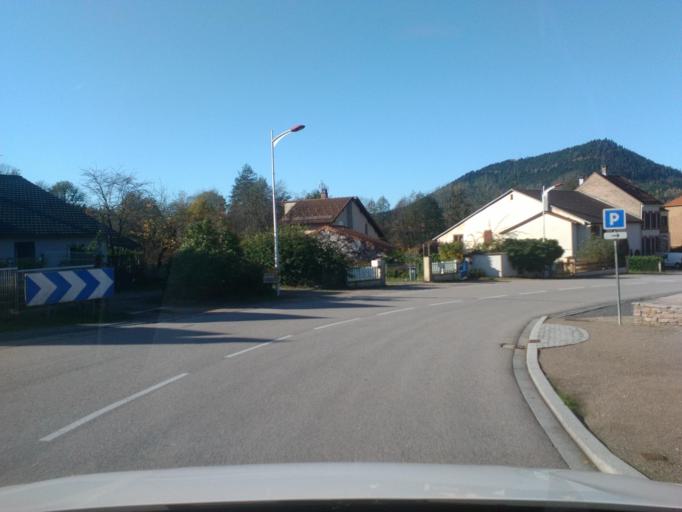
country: FR
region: Lorraine
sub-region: Departement des Vosges
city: Senones
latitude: 48.4083
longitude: 7.0523
